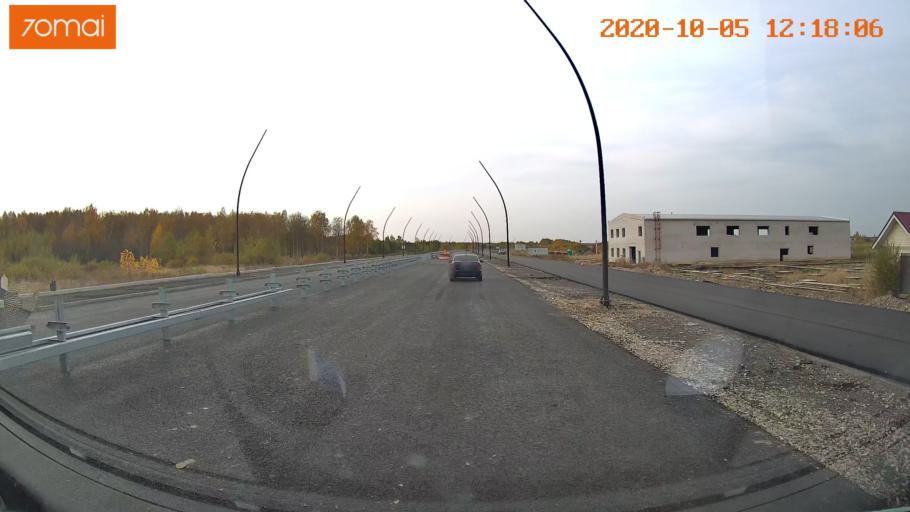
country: RU
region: Ivanovo
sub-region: Gorod Ivanovo
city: Ivanovo
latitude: 56.9526
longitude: 40.9465
